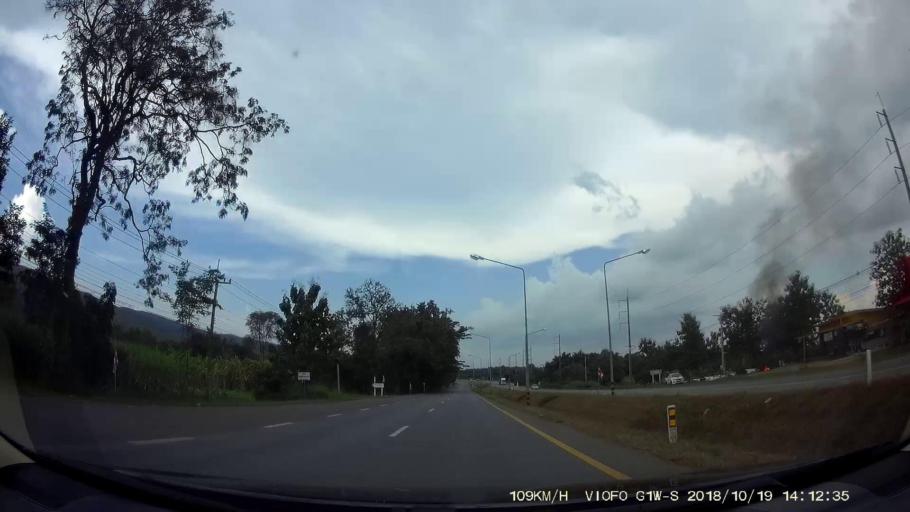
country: TH
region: Chaiyaphum
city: Khon Sawan
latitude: 15.9497
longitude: 102.1750
